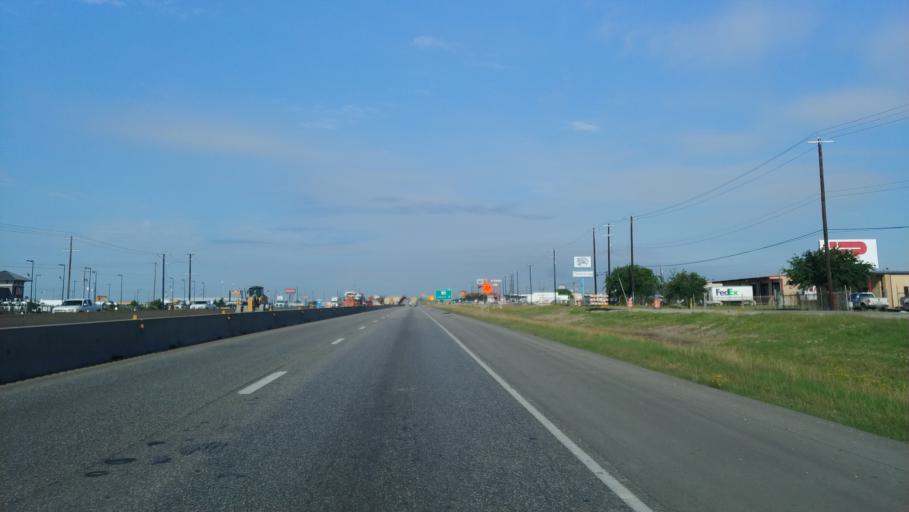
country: US
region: Texas
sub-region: Bexar County
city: Converse
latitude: 29.4609
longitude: -98.3098
